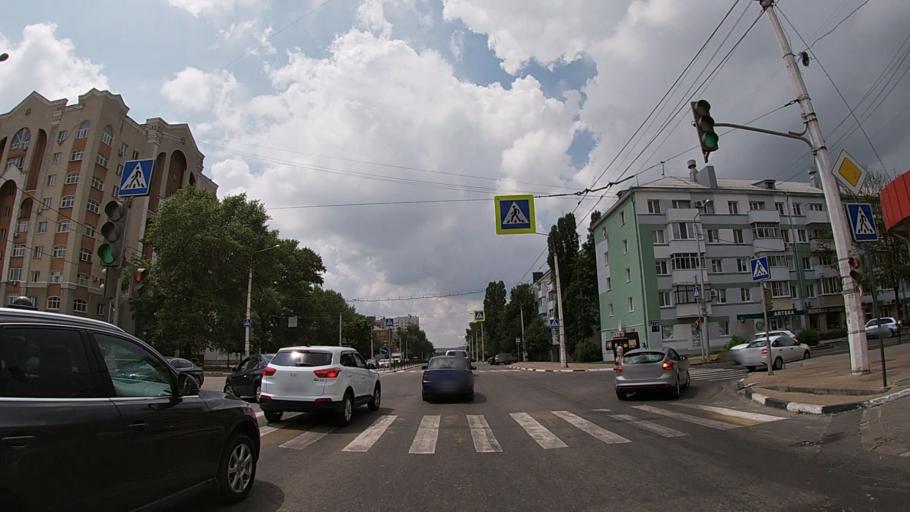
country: RU
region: Belgorod
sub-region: Belgorodskiy Rayon
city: Belgorod
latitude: 50.6124
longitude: 36.5841
